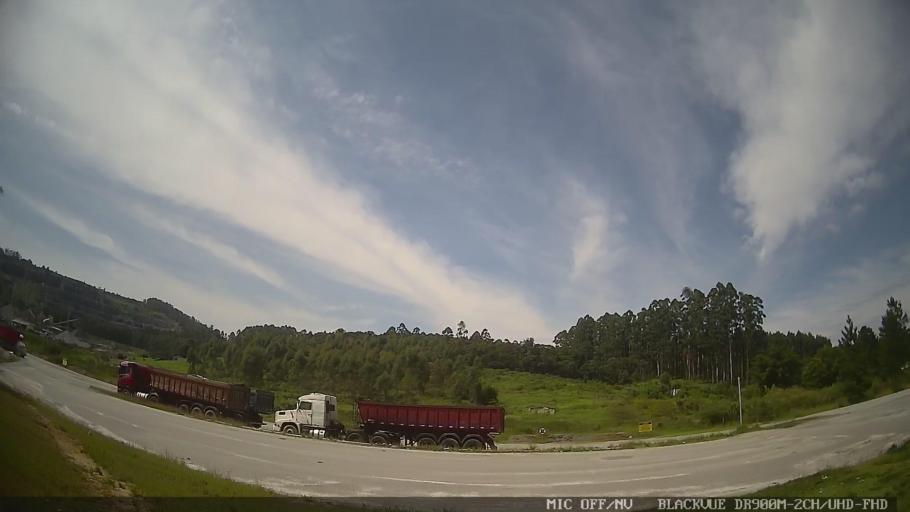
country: BR
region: Sao Paulo
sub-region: Mogi das Cruzes
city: Mogi das Cruzes
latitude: -23.4952
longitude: -46.2545
